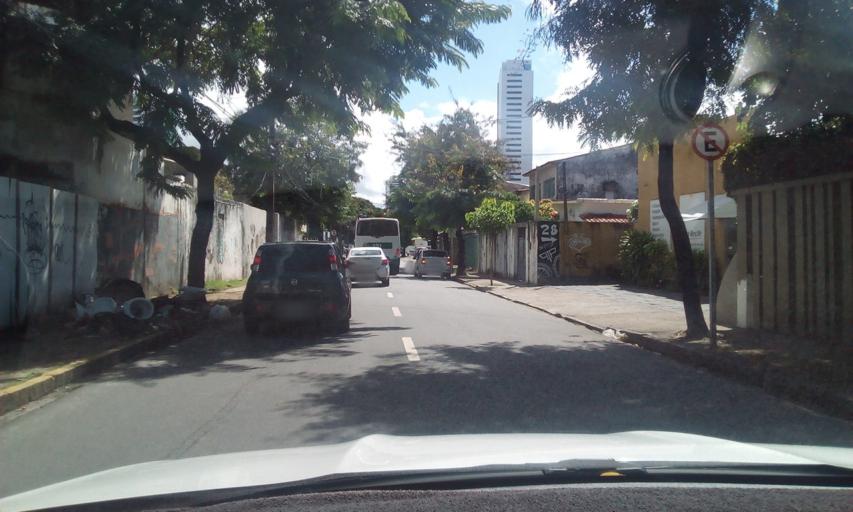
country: BR
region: Pernambuco
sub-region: Recife
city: Recife
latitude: -8.0511
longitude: -34.8884
